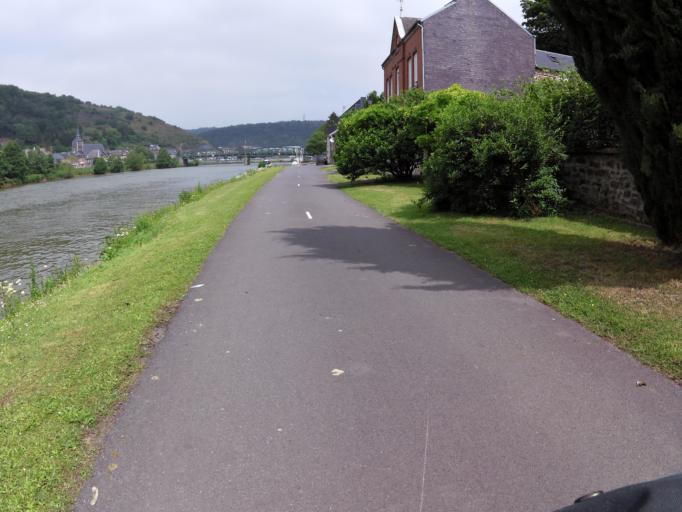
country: FR
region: Champagne-Ardenne
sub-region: Departement des Ardennes
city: Vireux-Wallerand
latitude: 50.0824
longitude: 4.7270
